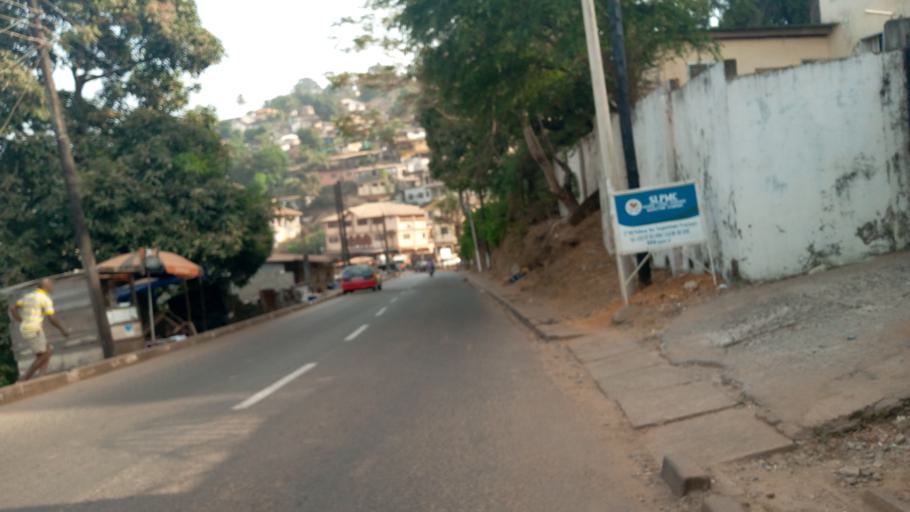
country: SL
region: Western Area
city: Freetown
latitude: 8.4765
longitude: -13.2585
